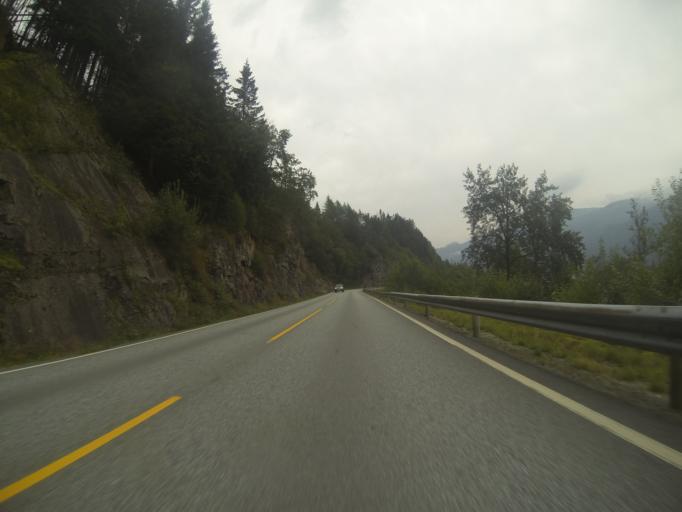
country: NO
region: Rogaland
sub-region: Suldal
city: Sand
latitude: 59.5670
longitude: 6.2743
